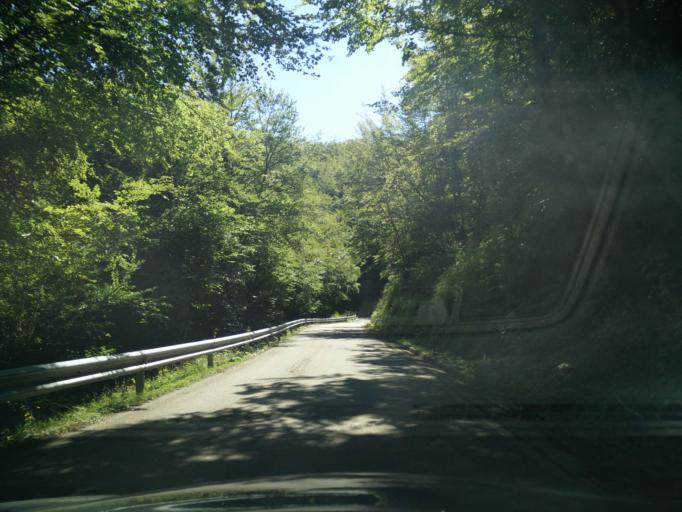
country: ES
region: Asturias
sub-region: Province of Asturias
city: Amieva
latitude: 43.1953
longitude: -5.1461
